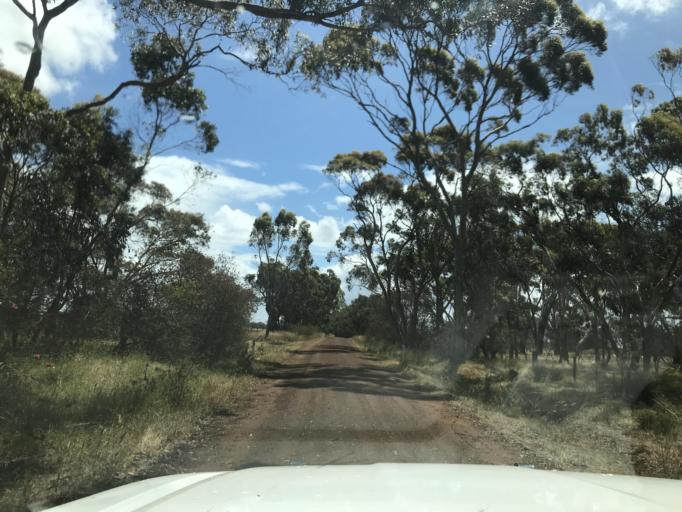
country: AU
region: South Australia
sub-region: Wattle Range
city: Penola
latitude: -37.1248
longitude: 141.2944
